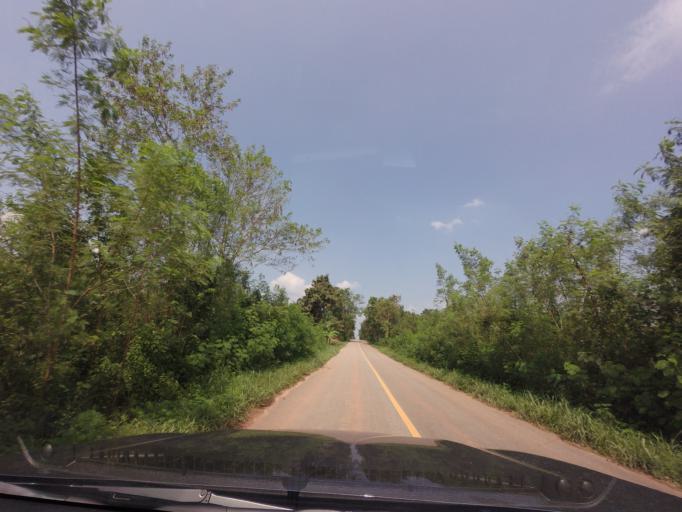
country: TH
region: Uttaradit
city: Fak Tha
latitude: 17.8600
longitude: 100.9648
